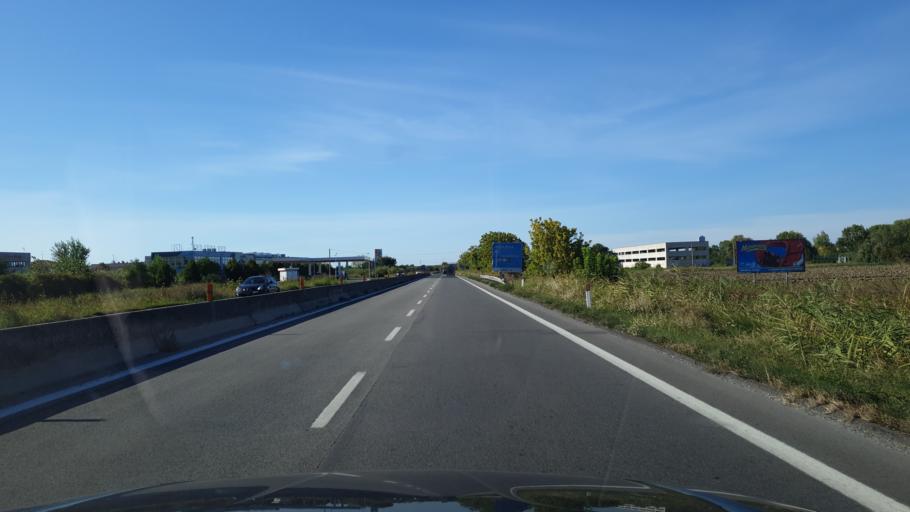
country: IT
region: Emilia-Romagna
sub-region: Forli-Cesena
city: Gatteo a Mare
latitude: 44.1738
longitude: 12.4182
